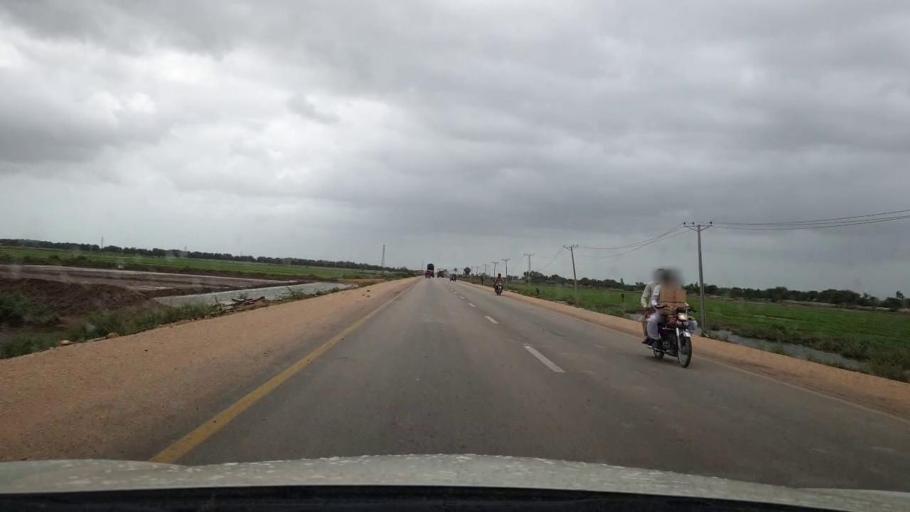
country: PK
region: Sindh
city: Badin
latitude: 24.6557
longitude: 68.7195
